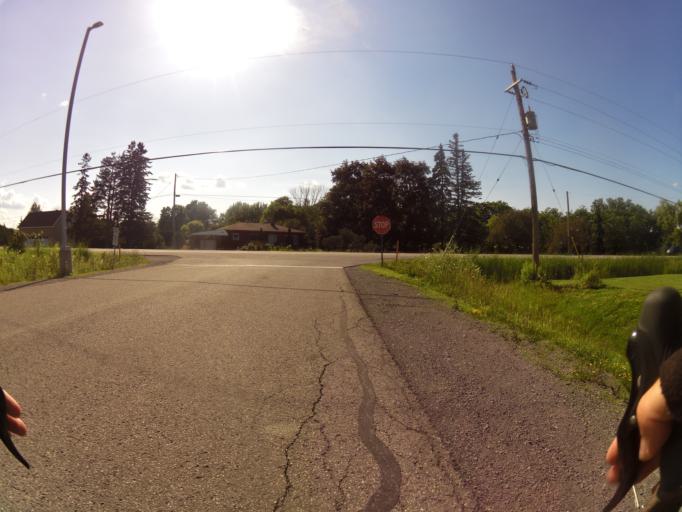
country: CA
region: Ontario
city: Ottawa
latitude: 45.3153
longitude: -75.6921
